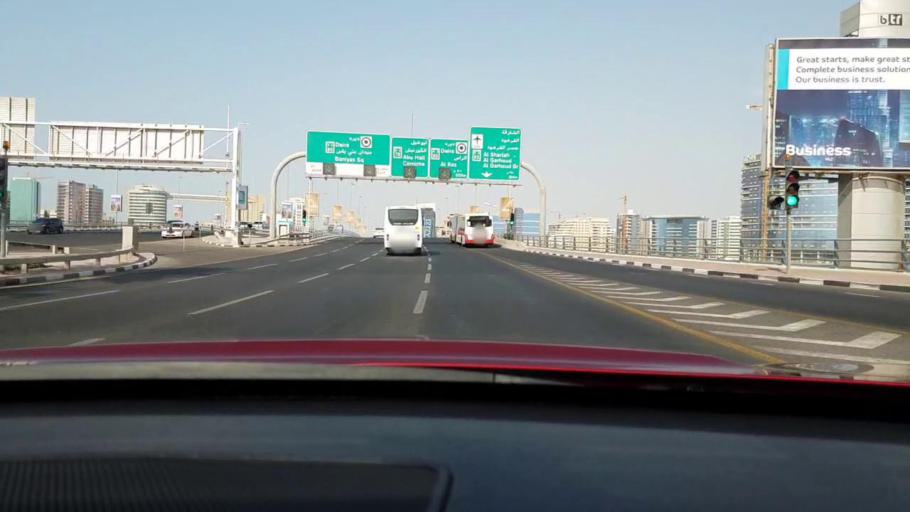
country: AE
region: Ash Shariqah
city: Sharjah
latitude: 25.2505
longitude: 55.3201
